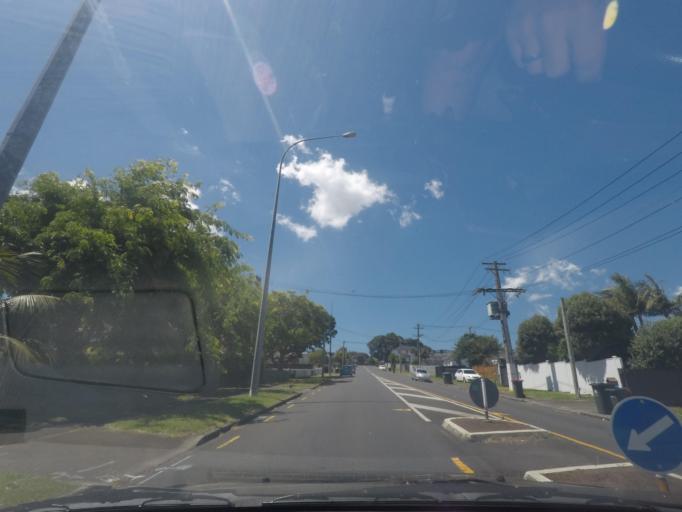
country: NZ
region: Auckland
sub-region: Auckland
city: Auckland
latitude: -36.9132
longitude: 174.7552
